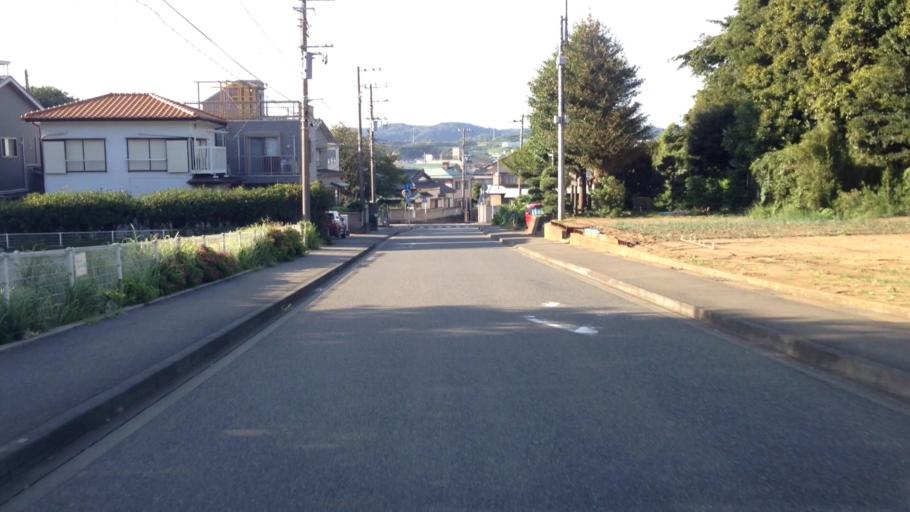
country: JP
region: Kanagawa
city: Miura
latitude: 35.2059
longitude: 139.6156
